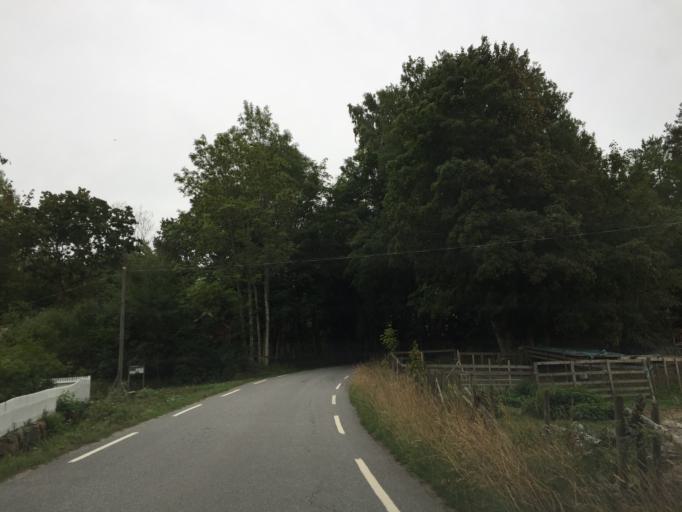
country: NO
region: Ostfold
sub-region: Hvaler
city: Skjaerhalden
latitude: 59.0752
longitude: 11.0046
